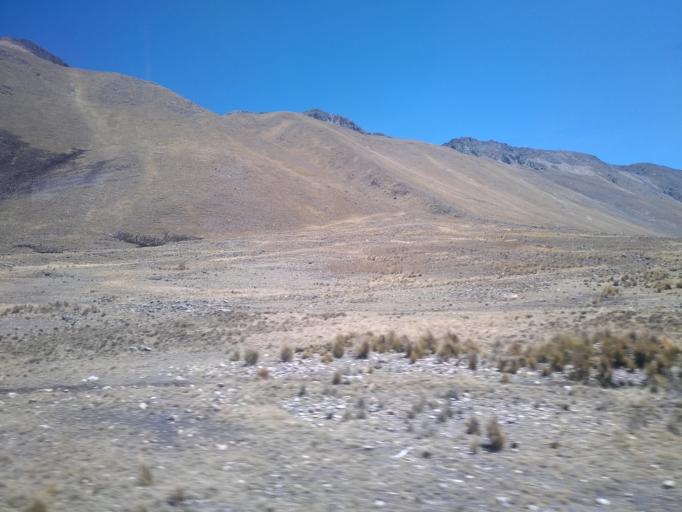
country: PE
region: Cusco
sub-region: Provincia de Canas
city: Layo
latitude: -14.4788
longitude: -71.0090
